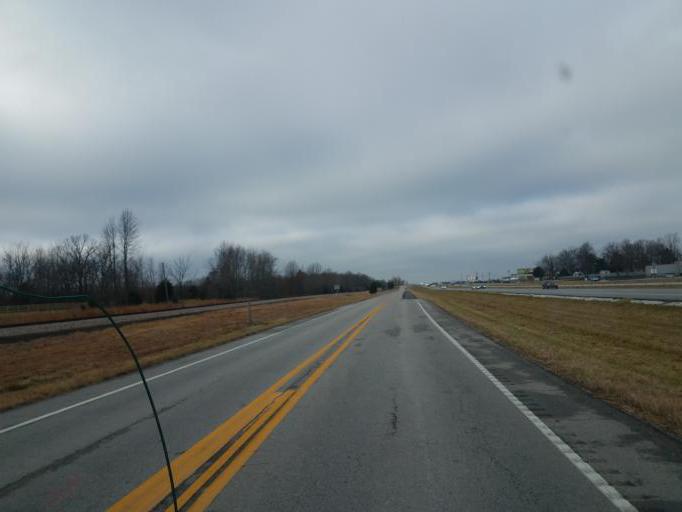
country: US
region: Missouri
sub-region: Greene County
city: Strafford
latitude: 37.2716
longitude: -93.0605
